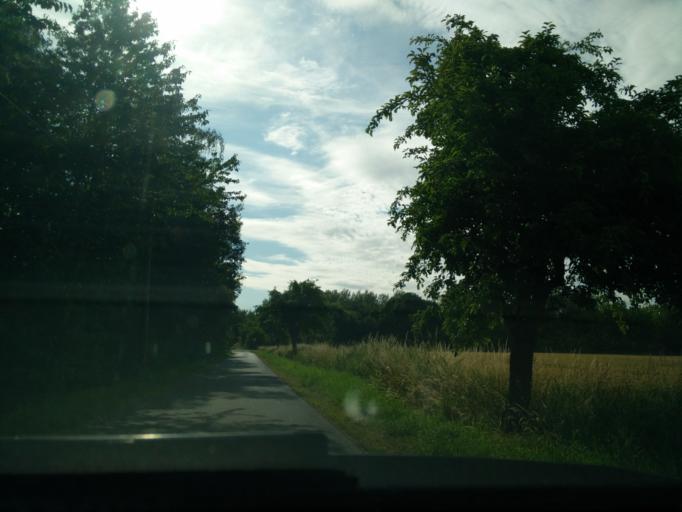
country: DE
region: Saxony
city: Geithain
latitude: 51.0719
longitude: 12.6925
